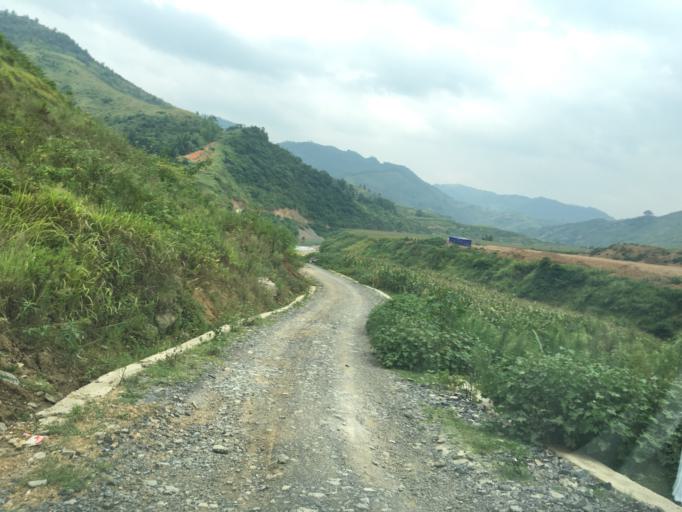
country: CN
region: Guangxi Zhuangzu Zizhiqu
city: Xinzhou
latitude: 25.1885
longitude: 105.7320
